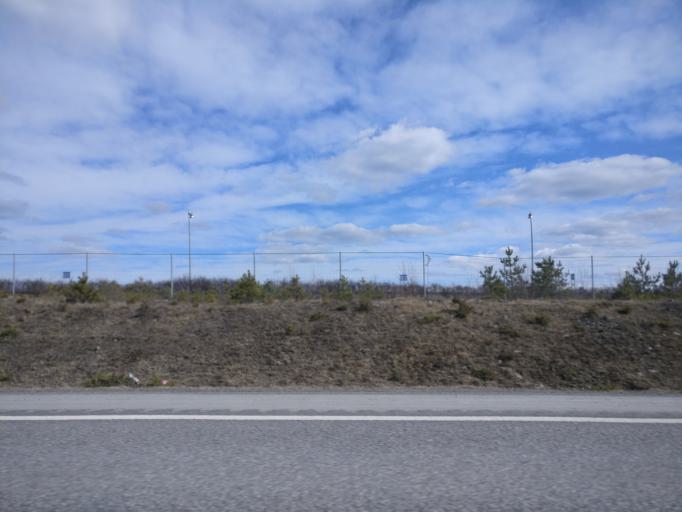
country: FI
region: Pirkanmaa
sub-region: Tampere
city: Lempaeaelae
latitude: 61.3585
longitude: 23.7921
